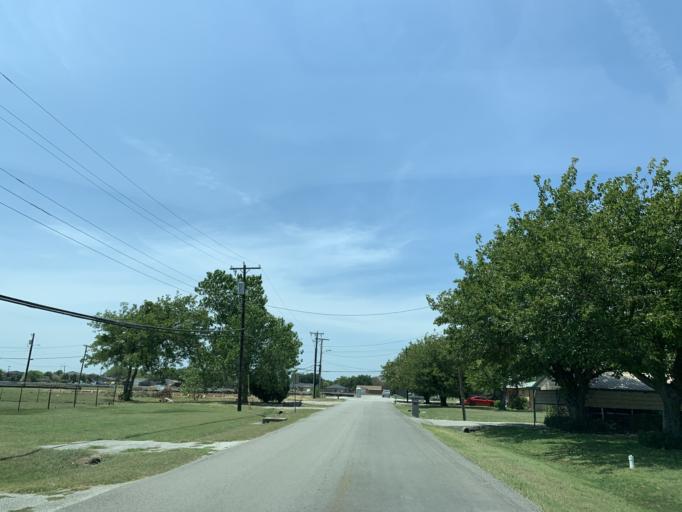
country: US
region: Texas
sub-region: Dallas County
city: Cedar Hill
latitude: 32.6475
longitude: -97.0267
